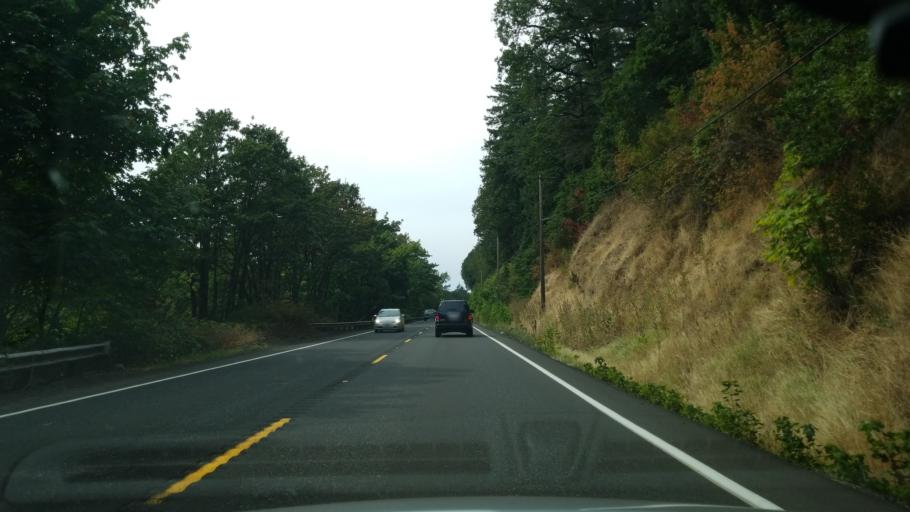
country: US
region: Washington
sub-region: Clark County
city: Washougal
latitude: 45.5621
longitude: -122.2686
